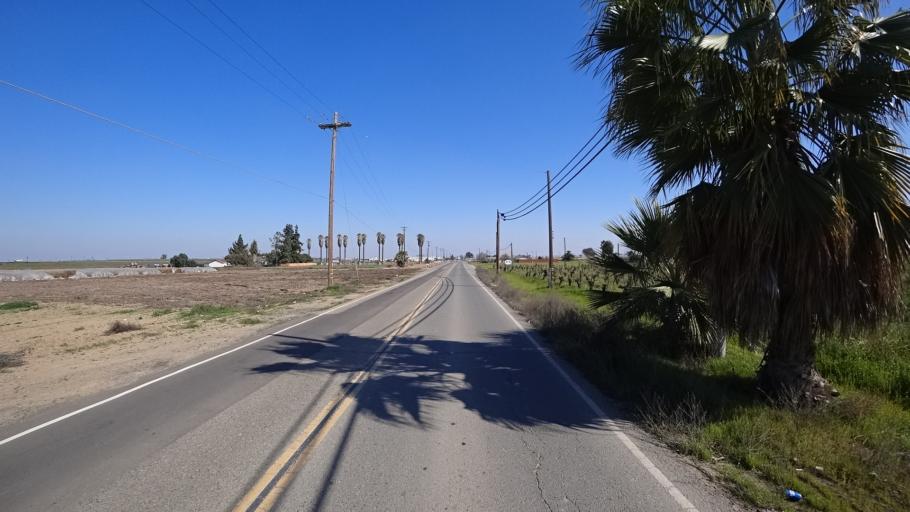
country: US
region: California
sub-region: Fresno County
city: West Park
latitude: 36.7356
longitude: -119.8498
